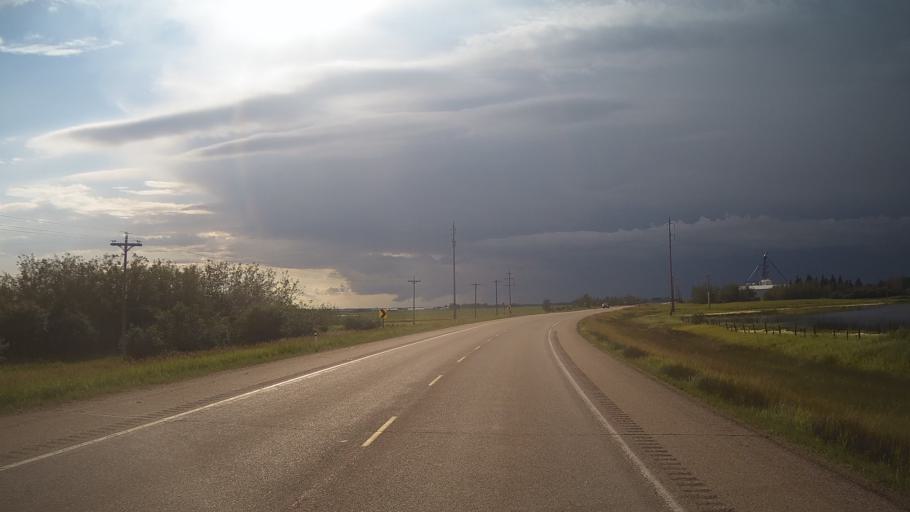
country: CA
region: Alberta
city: Vegreville
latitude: 53.2220
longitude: -112.2183
